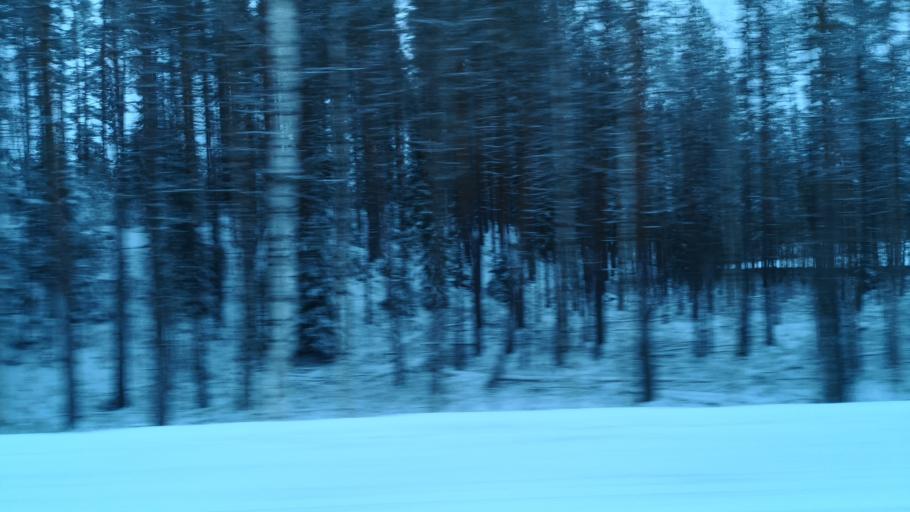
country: FI
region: Southern Savonia
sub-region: Savonlinna
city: Savonlinna
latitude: 61.9812
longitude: 28.8103
